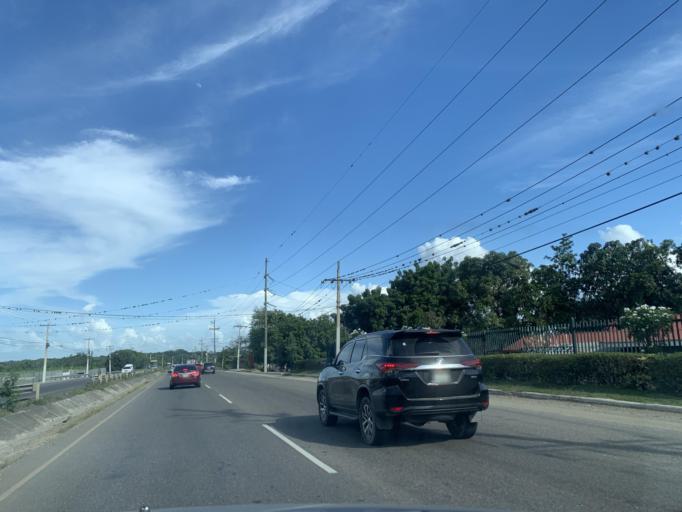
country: DO
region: Santiago
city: Villa Gonzalez
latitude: 19.5279
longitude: -70.7742
